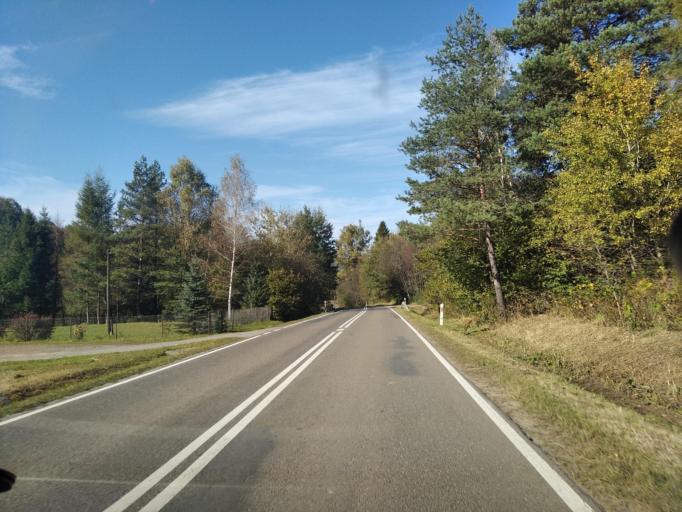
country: PL
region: Subcarpathian Voivodeship
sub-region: Powiat leski
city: Baligrod
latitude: 49.2726
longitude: 22.2881
